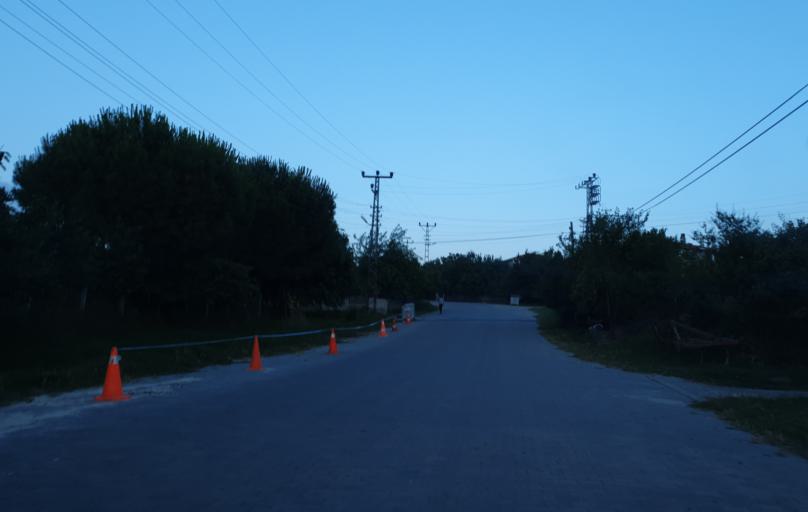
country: TR
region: Tekirdag
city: Velimese
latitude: 41.3498
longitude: 27.8808
